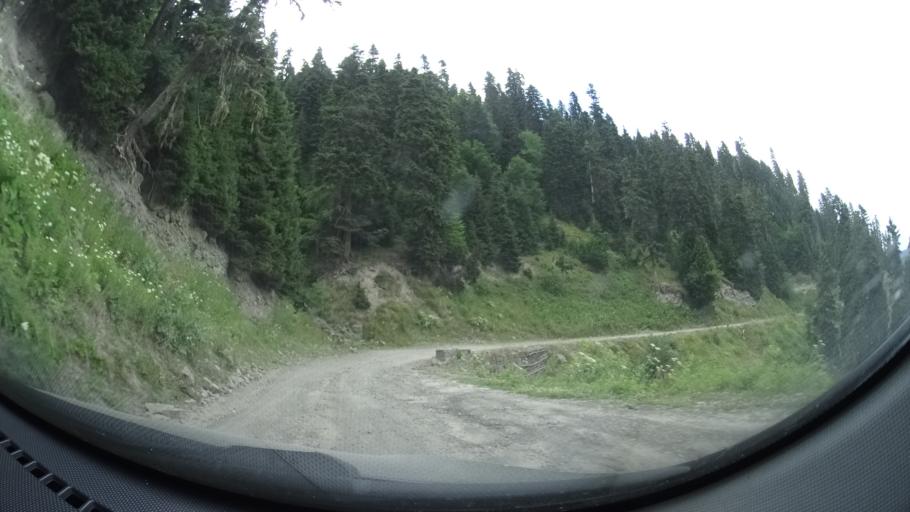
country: GE
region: Samtskhe-Javakheti
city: Adigeni
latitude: 41.6367
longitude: 42.5795
